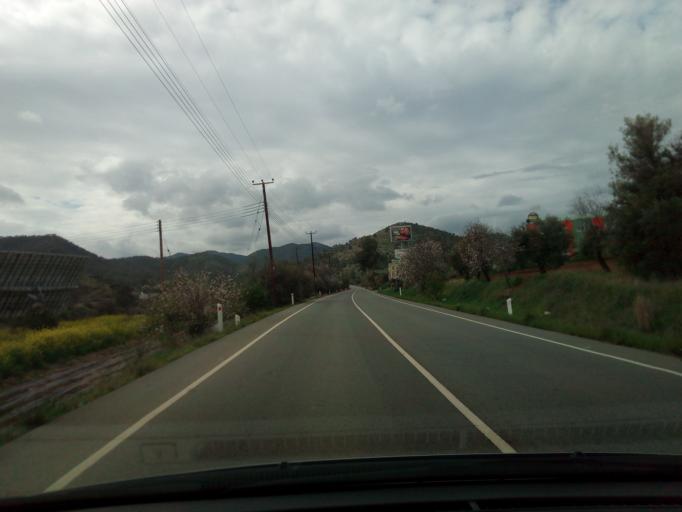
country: CY
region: Lefkosia
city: Klirou
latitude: 35.0110
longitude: 33.1502
